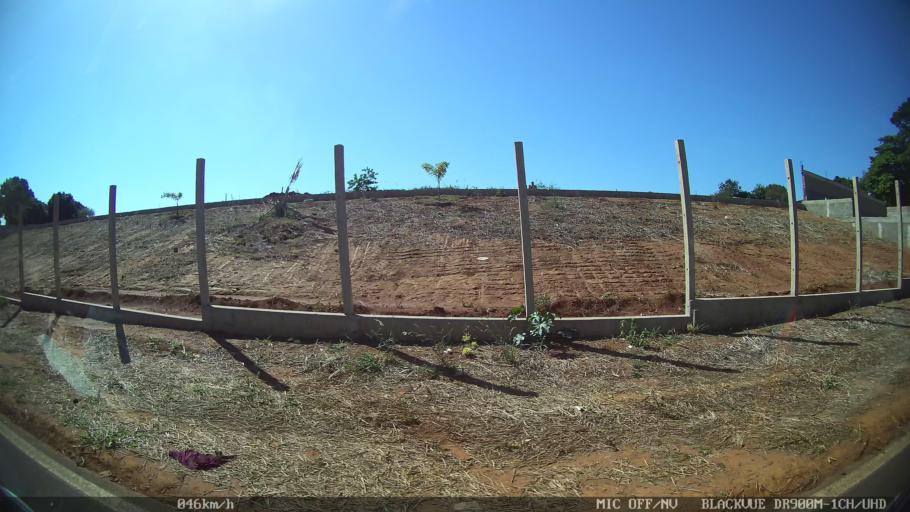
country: BR
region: Sao Paulo
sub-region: Batatais
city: Batatais
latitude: -20.8800
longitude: -47.6035
